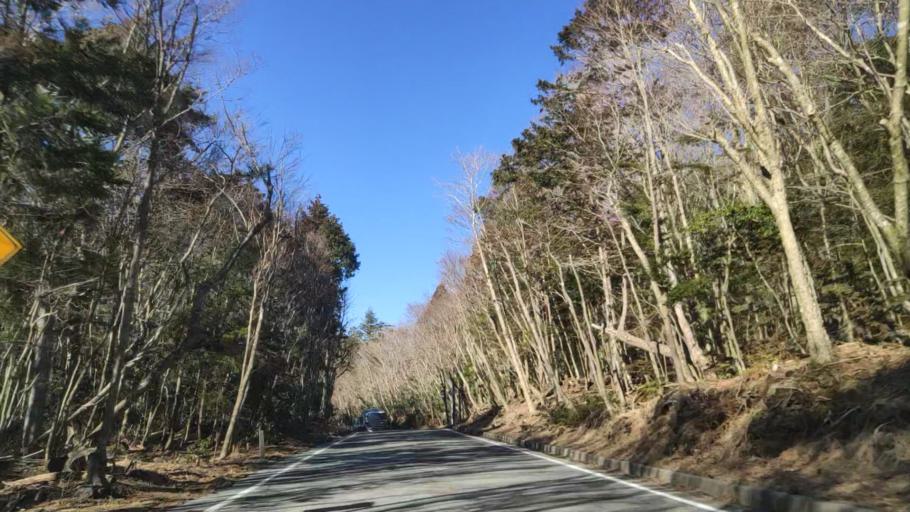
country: JP
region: Yamanashi
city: Fujikawaguchiko
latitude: 35.4478
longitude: 138.6414
